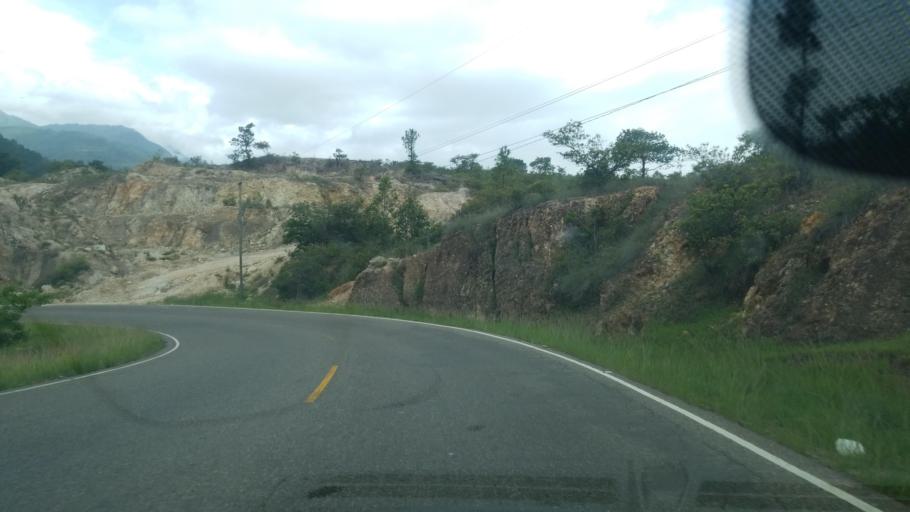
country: HN
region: Ocotepeque
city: Sinuapa
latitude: 14.4547
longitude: -89.1704
